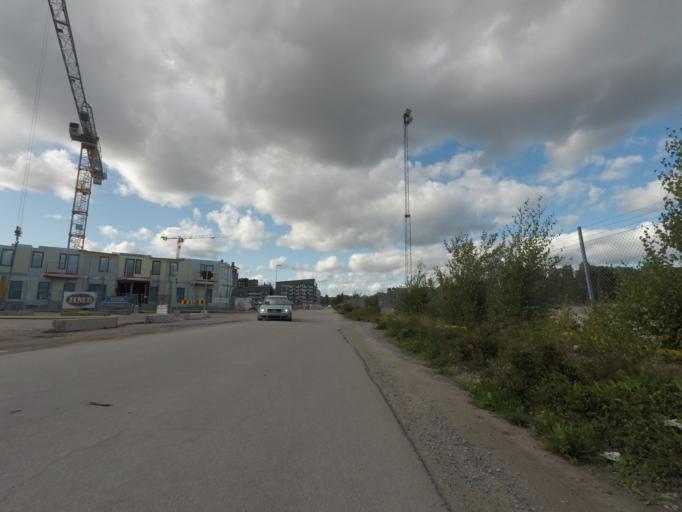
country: SE
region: Vaestmanland
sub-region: Vasteras
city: Vasteras
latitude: 59.6046
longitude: 16.5760
